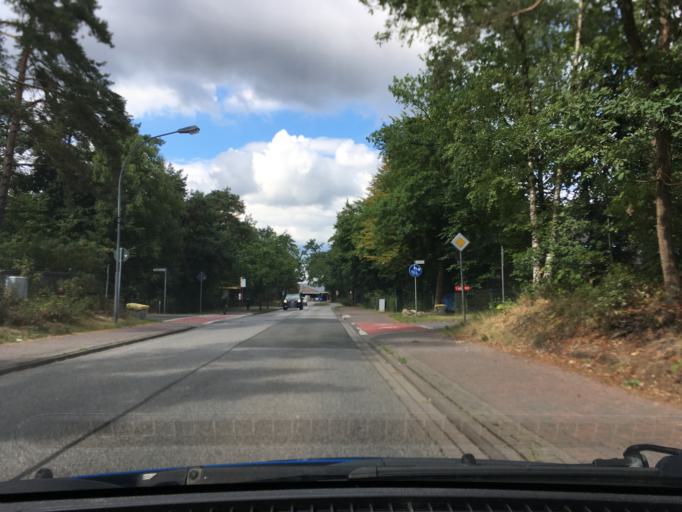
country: DE
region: Lower Saxony
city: Harmstorf
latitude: 53.3835
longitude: 10.0375
